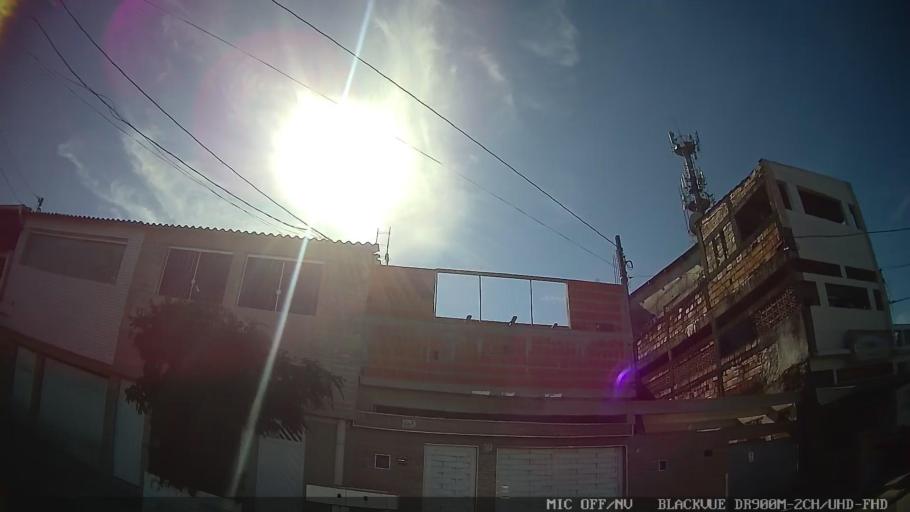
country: BR
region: Sao Paulo
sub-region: Santos
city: Santos
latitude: -23.9378
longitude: -46.2836
